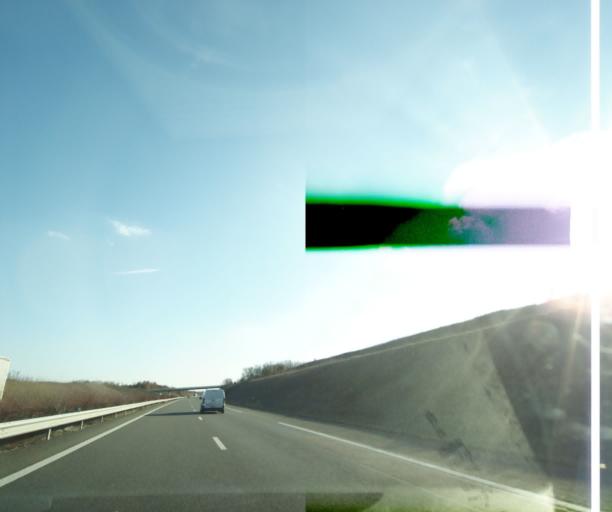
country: FR
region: Midi-Pyrenees
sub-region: Departement du Tarn-et-Garonne
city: Caussade
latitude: 44.2225
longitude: 1.5370
